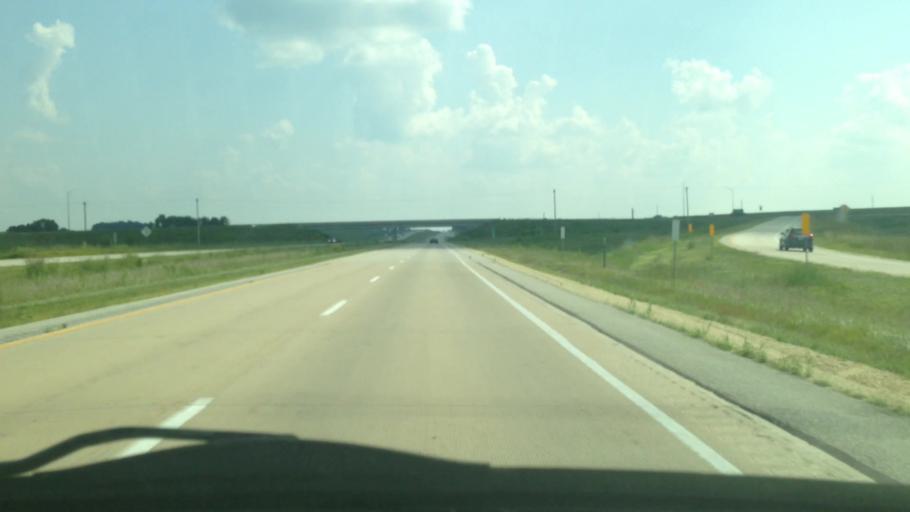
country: US
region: Iowa
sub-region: Bremer County
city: Denver
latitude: 42.7178
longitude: -92.3374
